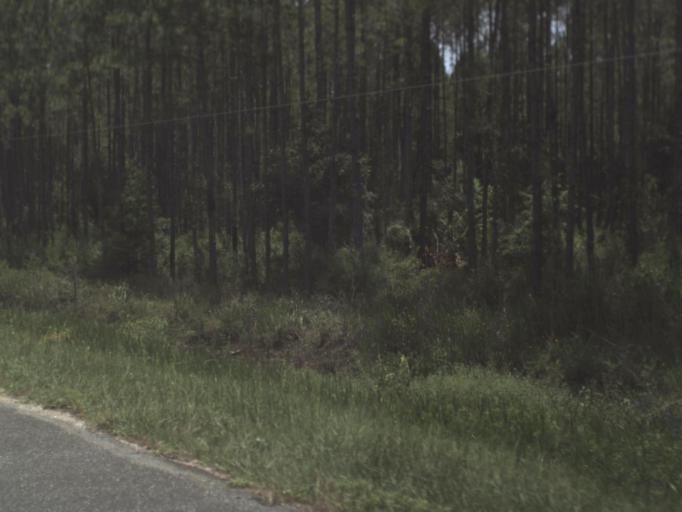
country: US
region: Florida
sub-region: Taylor County
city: Steinhatchee
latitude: 29.8283
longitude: -83.3144
